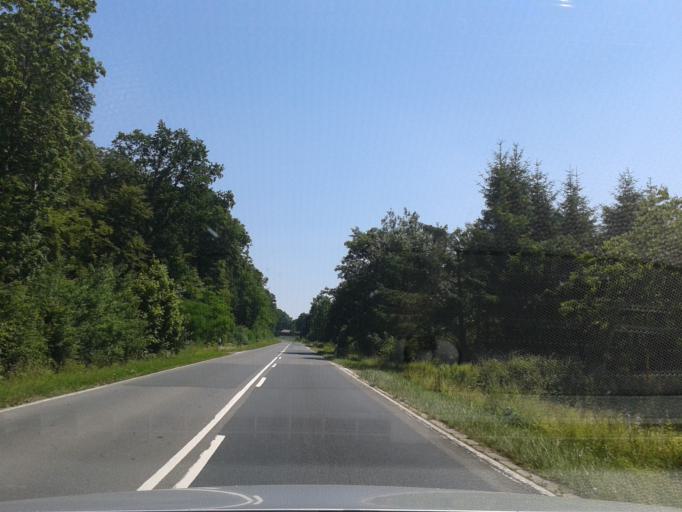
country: DE
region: North Rhine-Westphalia
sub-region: Regierungsbezirk Detmold
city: Barntrup
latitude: 51.9774
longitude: 9.1541
